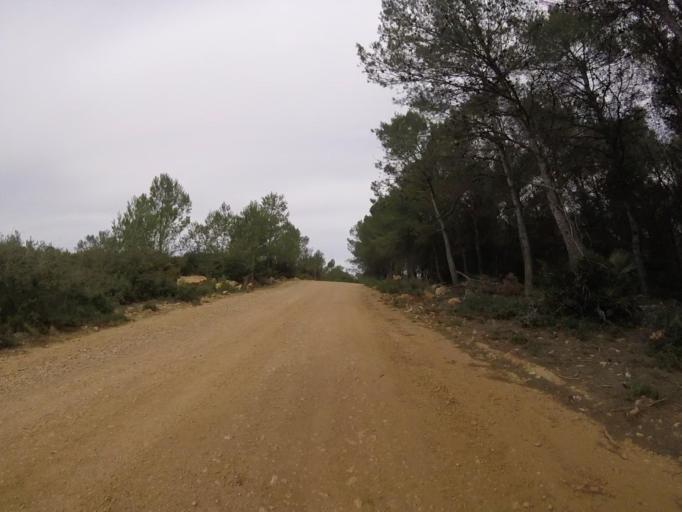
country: ES
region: Valencia
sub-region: Provincia de Castello
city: Benlloch
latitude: 40.1964
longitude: 0.0700
